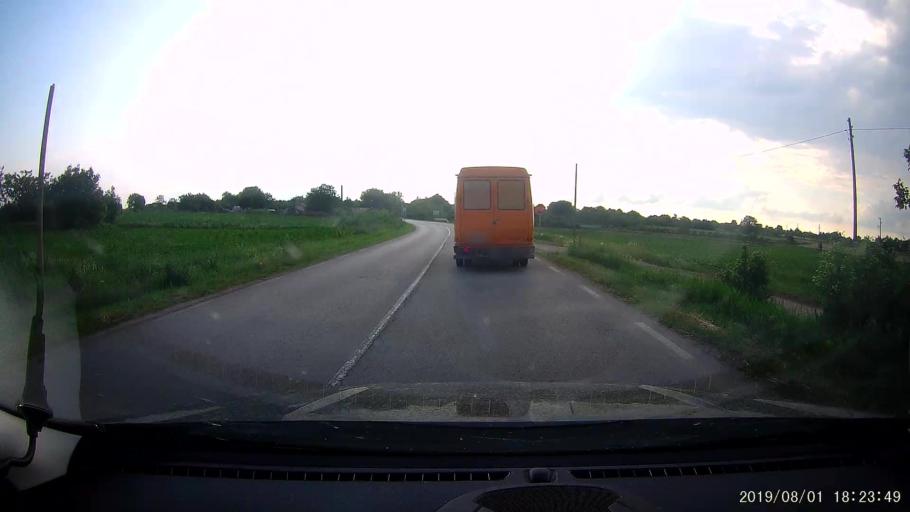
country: BG
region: Shumen
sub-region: Obshtina Kaolinovo
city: Kaolinovo
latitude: 43.6269
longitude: 27.0163
